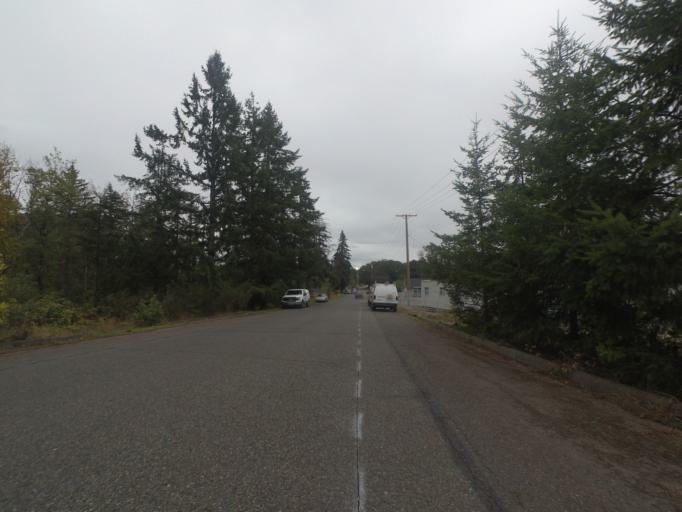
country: US
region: Washington
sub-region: Pierce County
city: McChord Air Force Base
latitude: 47.1491
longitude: -122.4992
